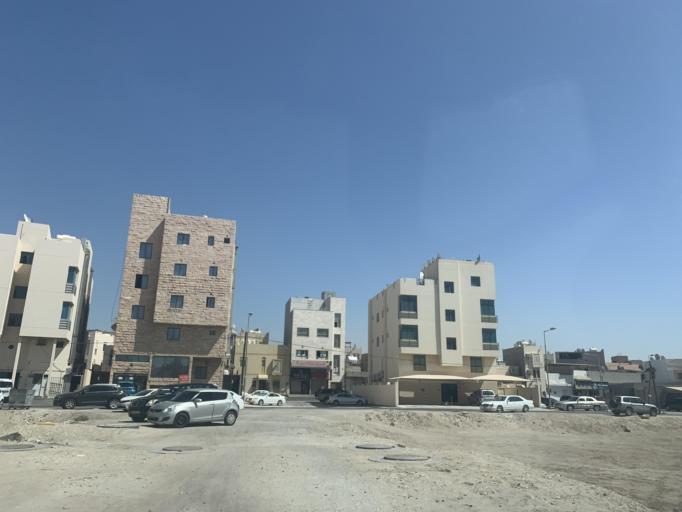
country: BH
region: Manama
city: Jidd Hafs
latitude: 26.2143
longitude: 50.5642
